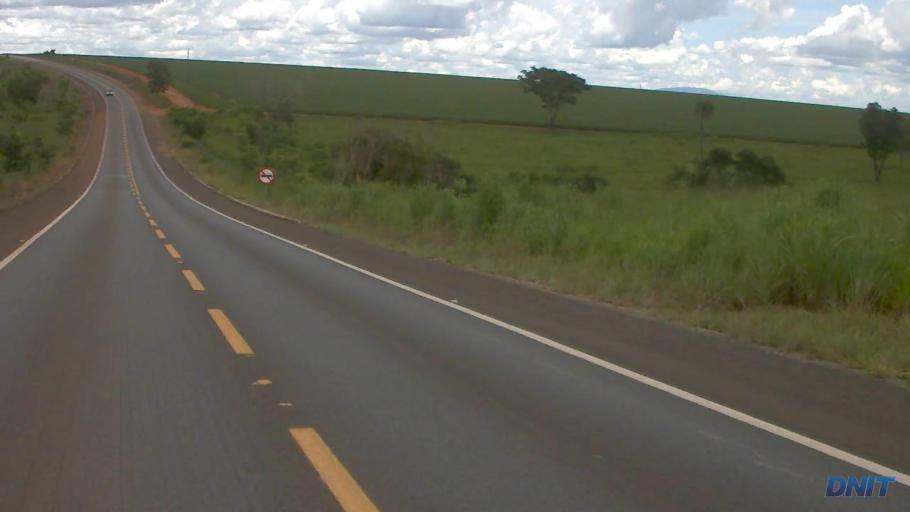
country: BR
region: Goias
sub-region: Uruacu
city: Uruacu
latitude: -14.6853
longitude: -49.1281
